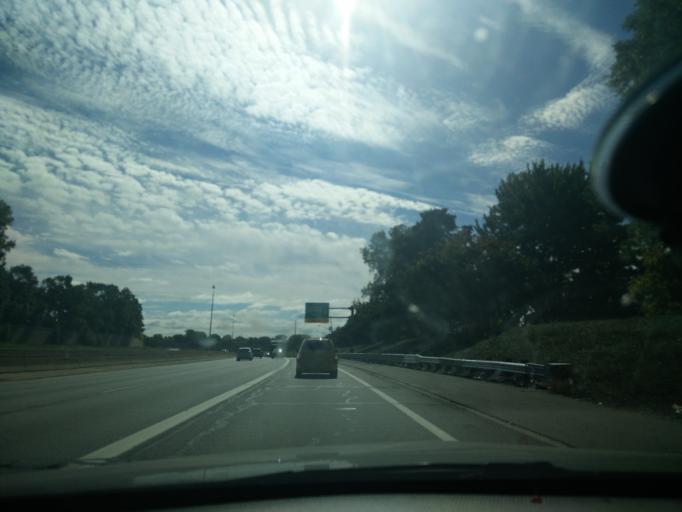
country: US
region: Michigan
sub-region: Macomb County
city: Roseville
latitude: 42.4849
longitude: -82.9176
